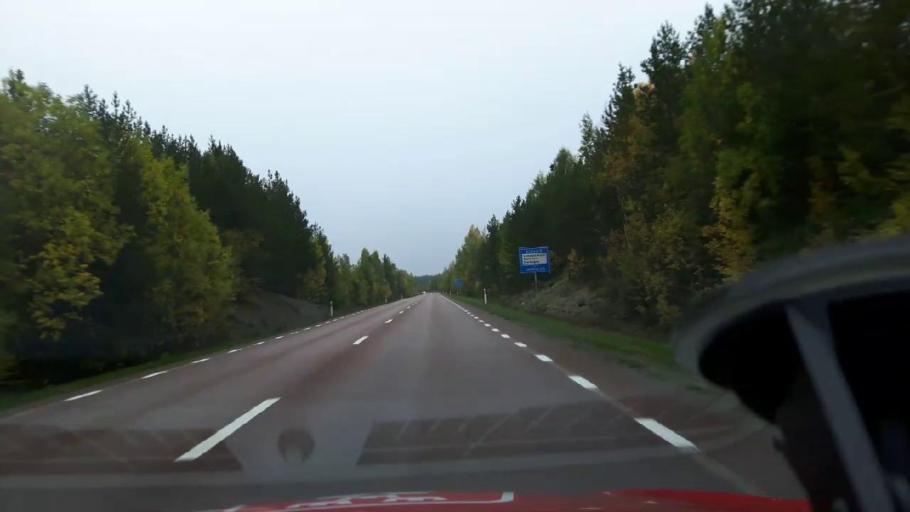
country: SE
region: Jaemtland
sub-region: Bergs Kommun
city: Hoverberg
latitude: 62.6265
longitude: 14.3706
